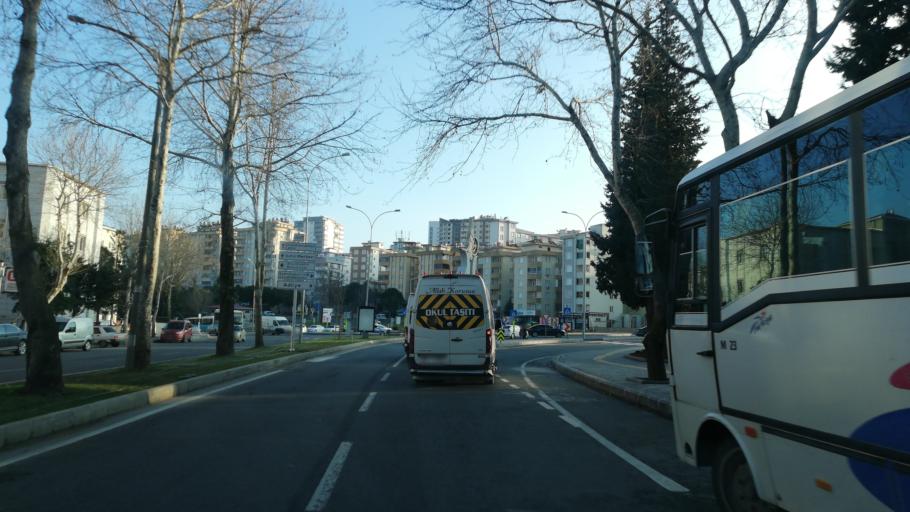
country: TR
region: Kahramanmaras
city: Kahramanmaras
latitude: 37.5857
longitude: 36.9042
